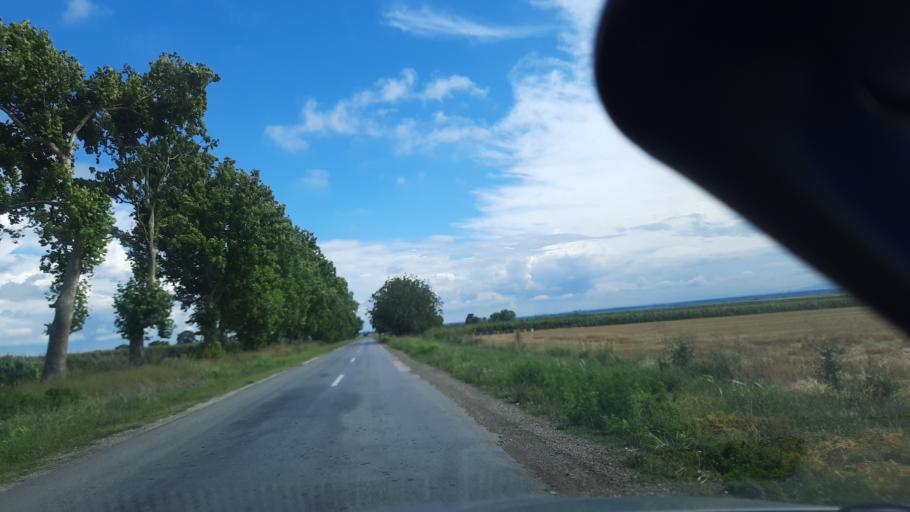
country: RS
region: Autonomna Pokrajina Vojvodina
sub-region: Sremski Okrug
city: Sremska Mitrovica
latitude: 45.0716
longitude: 19.5924
